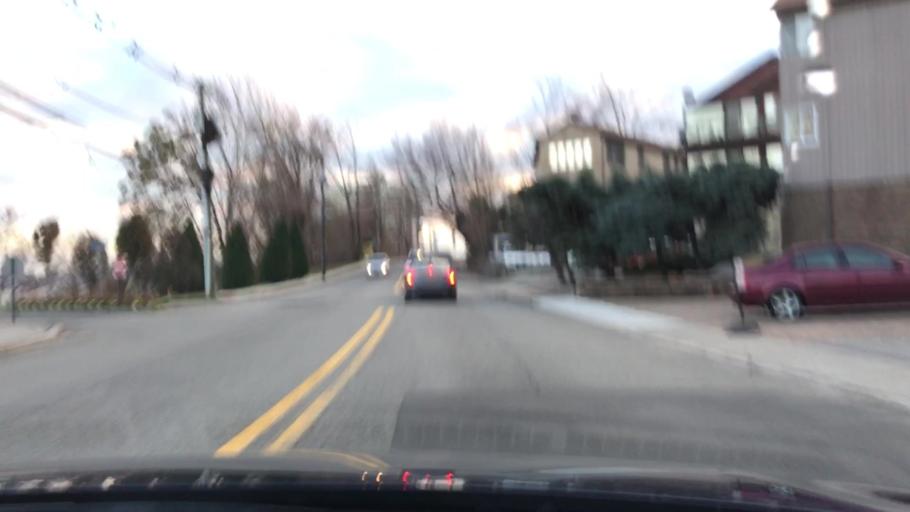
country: US
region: New Jersey
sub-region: Bergen County
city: Fort Lee
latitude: 40.8396
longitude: -73.9702
